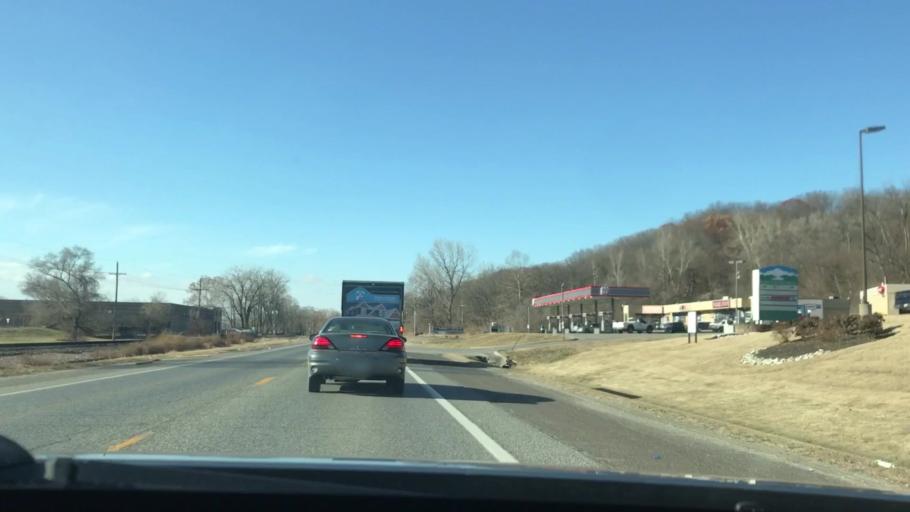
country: US
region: Missouri
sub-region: Platte County
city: Parkville
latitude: 39.1809
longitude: -94.6609
